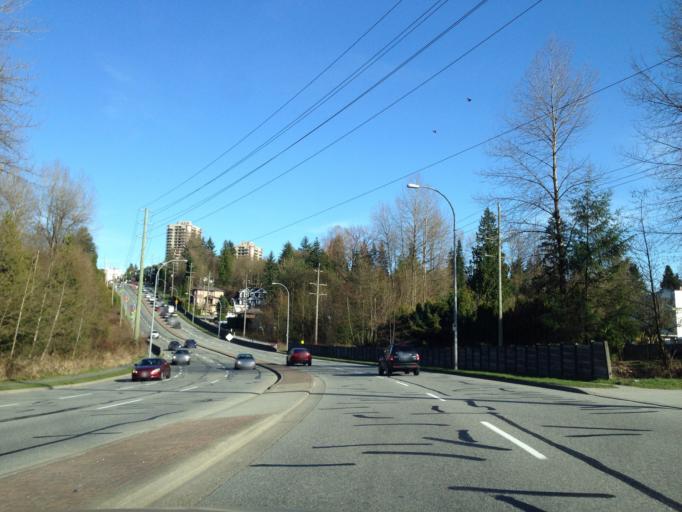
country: CA
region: British Columbia
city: Port Moody
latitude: 49.2633
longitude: -122.8992
